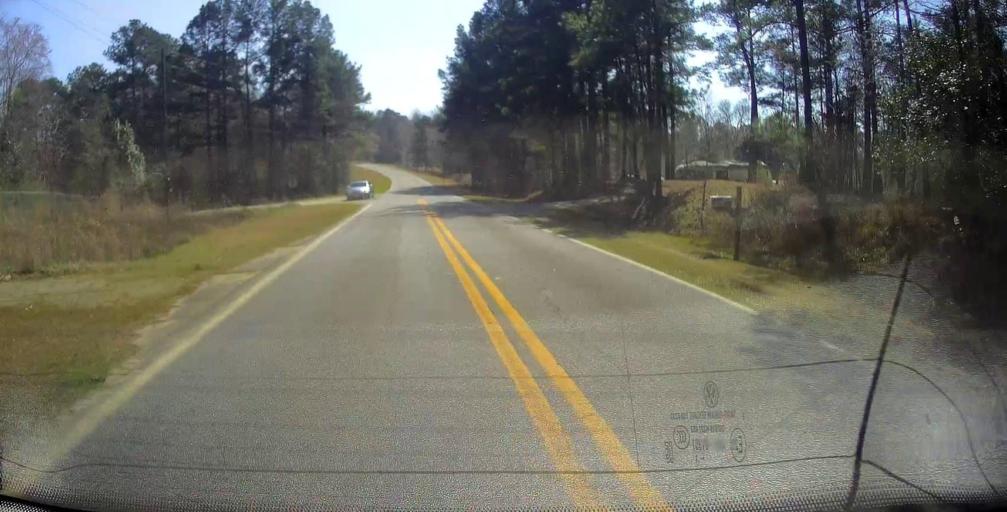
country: US
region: Georgia
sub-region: Jones County
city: Gray
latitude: 32.9346
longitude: -83.5358
